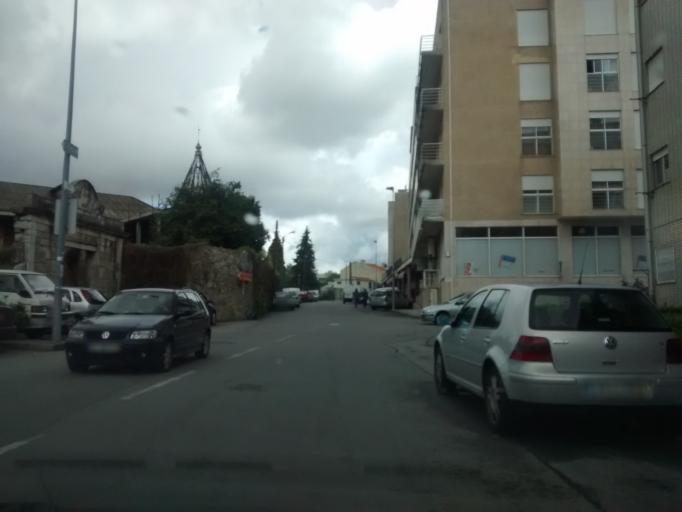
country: PT
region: Braga
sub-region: Braga
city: Braga
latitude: 41.5392
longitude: -8.4391
